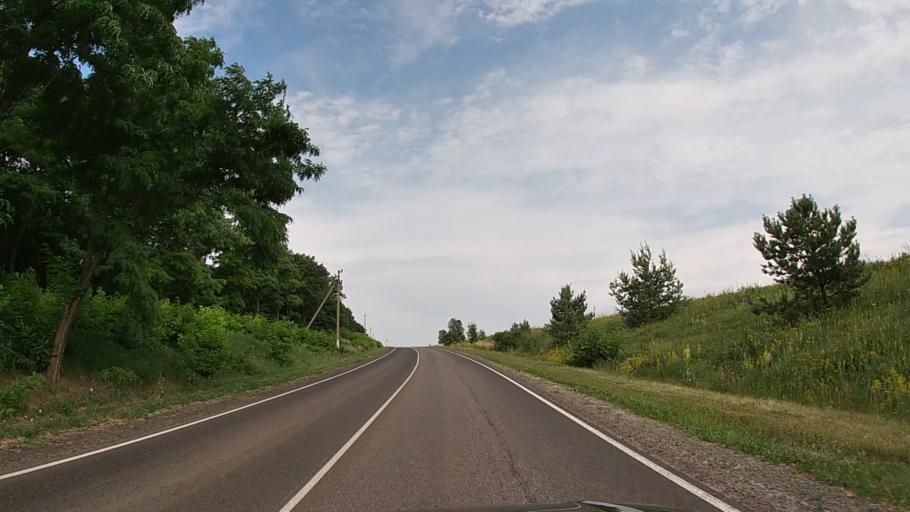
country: RU
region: Belgorod
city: Krasnaya Yaruga
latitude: 50.8302
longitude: 35.4948
